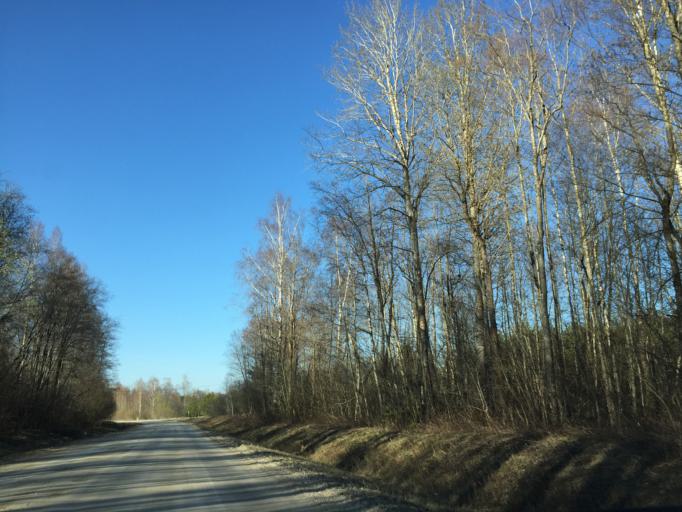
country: EE
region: Ida-Virumaa
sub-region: Sillamaee linn
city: Sillamae
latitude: 59.1040
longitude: 27.7952
